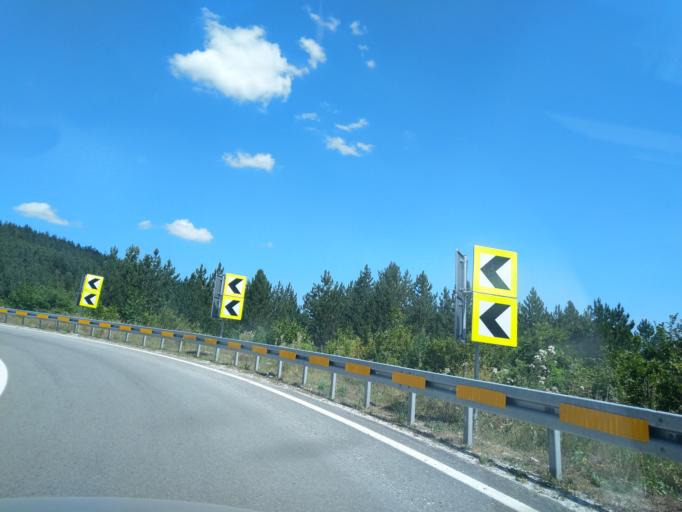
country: RS
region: Central Serbia
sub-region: Zlatiborski Okrug
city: Sjenica
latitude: 43.3082
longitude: 19.8999
